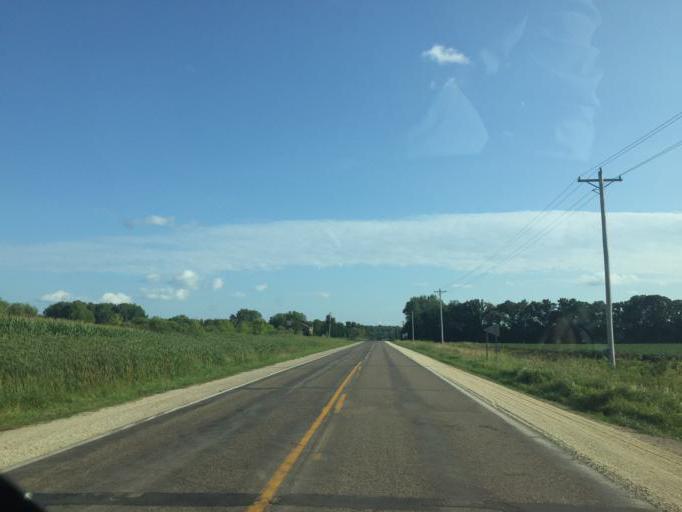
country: US
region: Minnesota
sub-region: Olmsted County
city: Rochester
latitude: 43.9661
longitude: -92.5581
